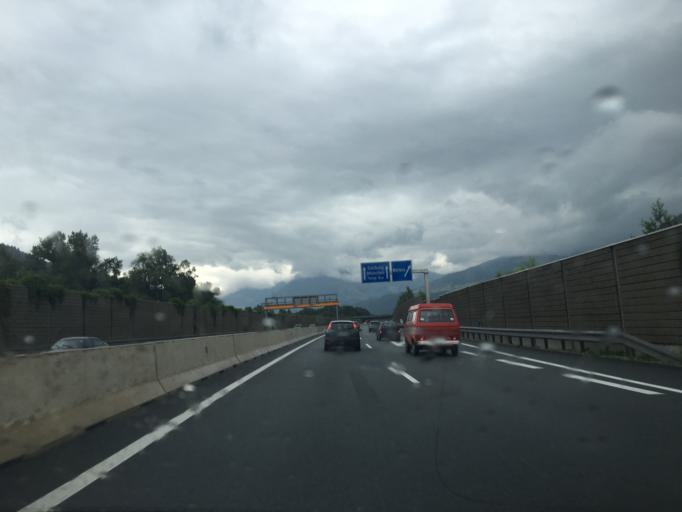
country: AT
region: Tyrol
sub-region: Politischer Bezirk Innsbruck Land
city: Fritzens
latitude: 47.2990
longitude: 11.5751
